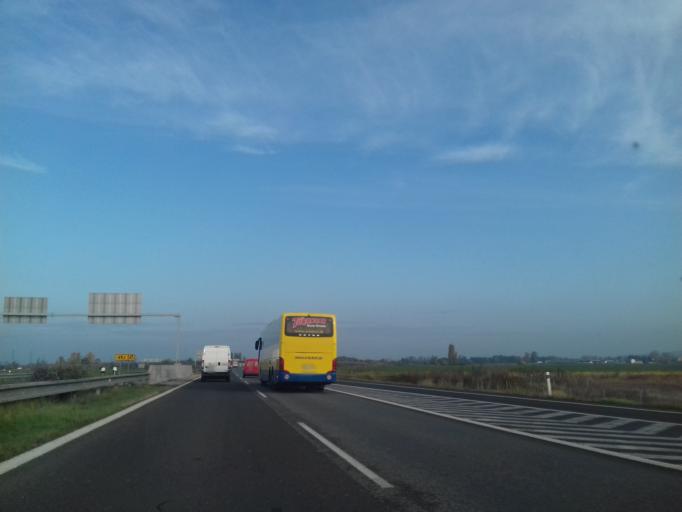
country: SK
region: Bratislavsky
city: Stupava
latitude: 48.2501
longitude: 17.0126
